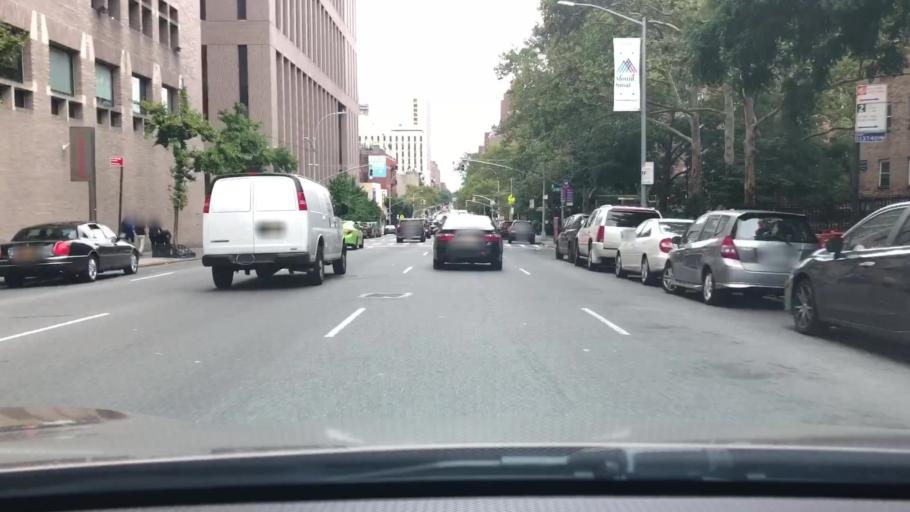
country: US
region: New York
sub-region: New York County
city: Manhattan
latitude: 40.7898
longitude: -73.9525
